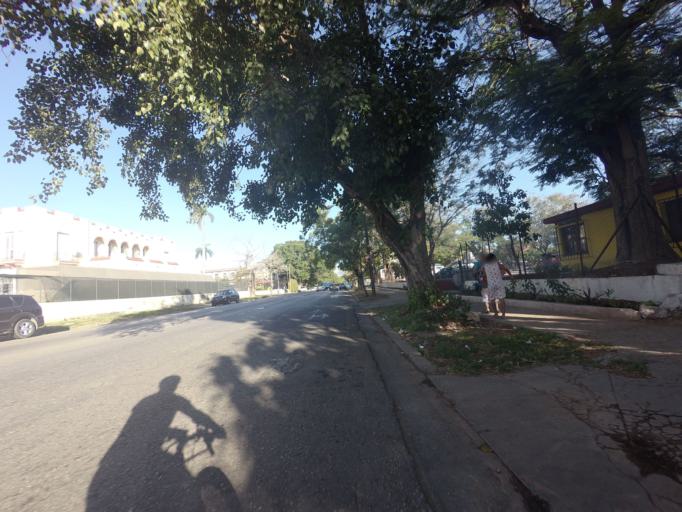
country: CU
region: La Habana
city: Havana
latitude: 23.1173
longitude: -82.4227
